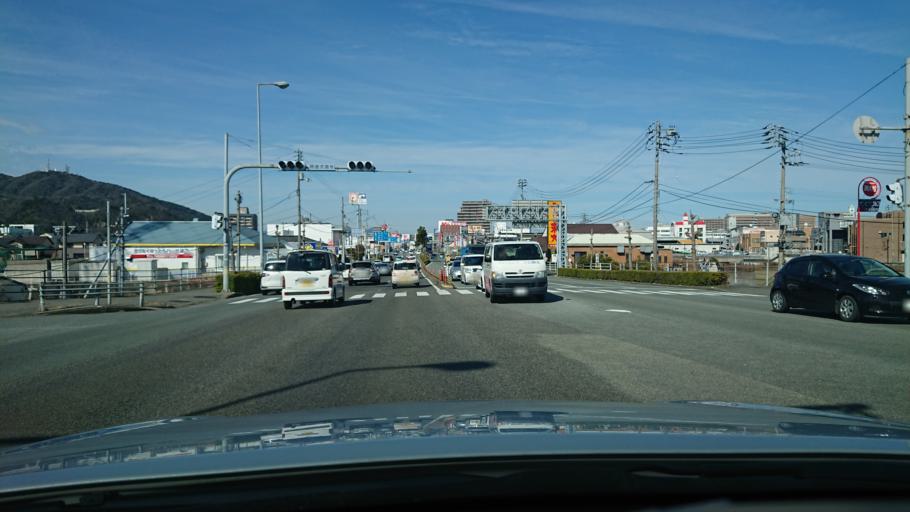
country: JP
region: Tokushima
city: Tokushima-shi
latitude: 34.0451
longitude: 134.5520
